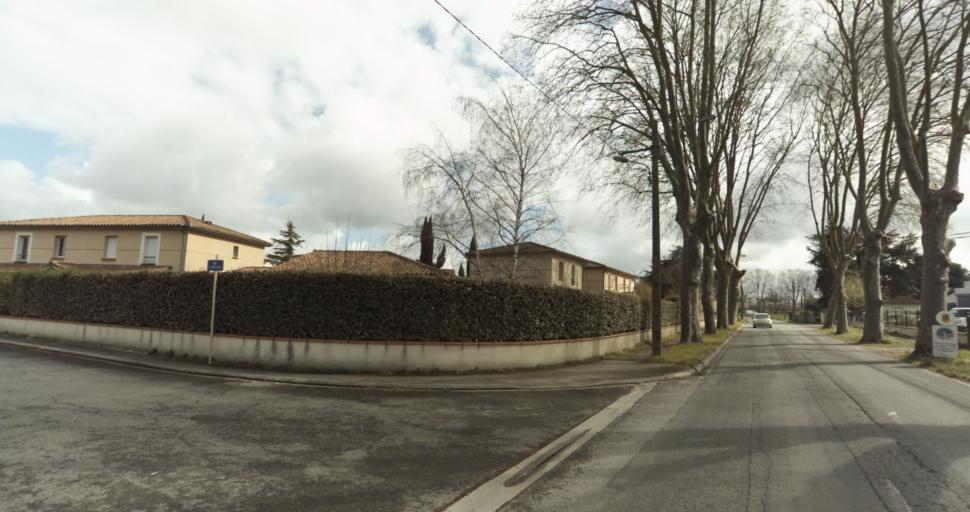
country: FR
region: Midi-Pyrenees
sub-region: Departement de la Haute-Garonne
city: Auterive
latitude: 43.3503
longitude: 1.4644
